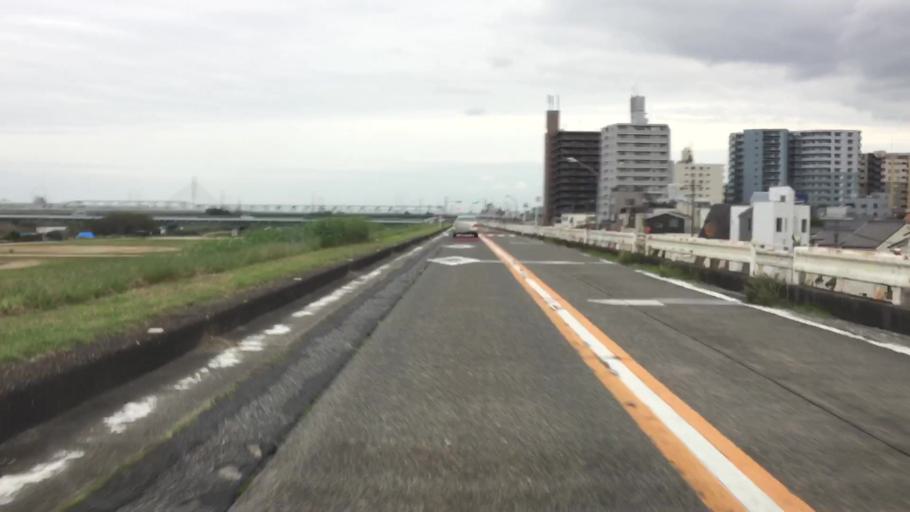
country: JP
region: Tokyo
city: Urayasu
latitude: 35.7328
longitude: 139.8248
